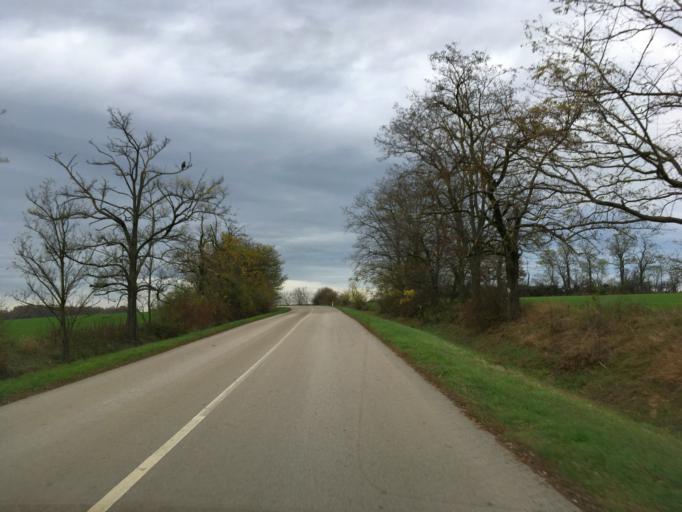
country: SK
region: Nitriansky
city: Svodin
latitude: 48.0280
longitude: 18.3995
